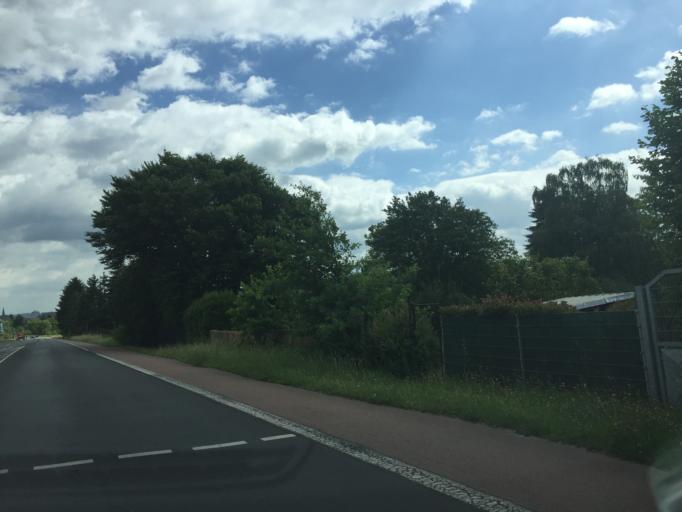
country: DE
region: Bavaria
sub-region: Regierungsbezirk Unterfranken
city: Aschaffenburg
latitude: 49.9628
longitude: 9.1294
